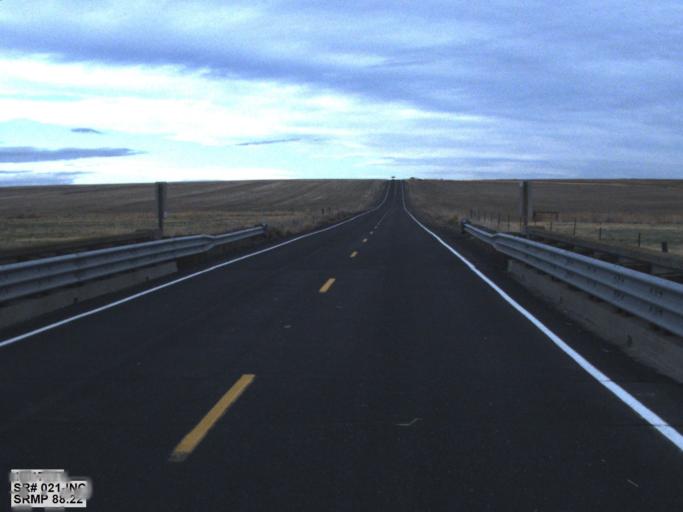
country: US
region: Washington
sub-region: Okanogan County
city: Coulee Dam
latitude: 47.7156
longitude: -118.7220
